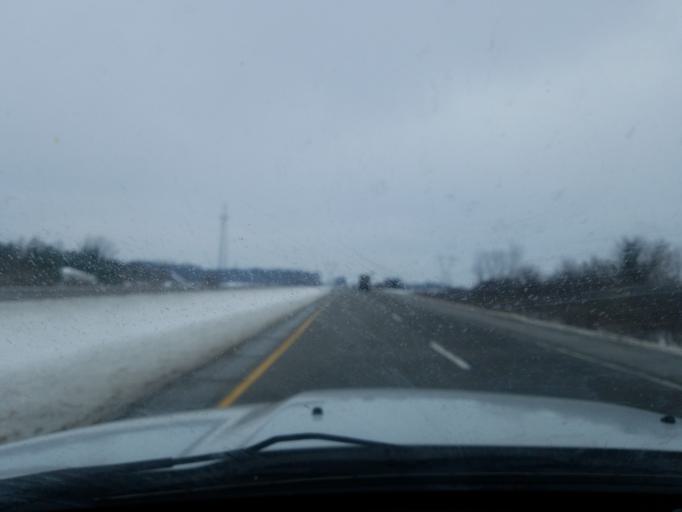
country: US
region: Indiana
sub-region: Marshall County
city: Argos
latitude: 41.1992
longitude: -86.2556
